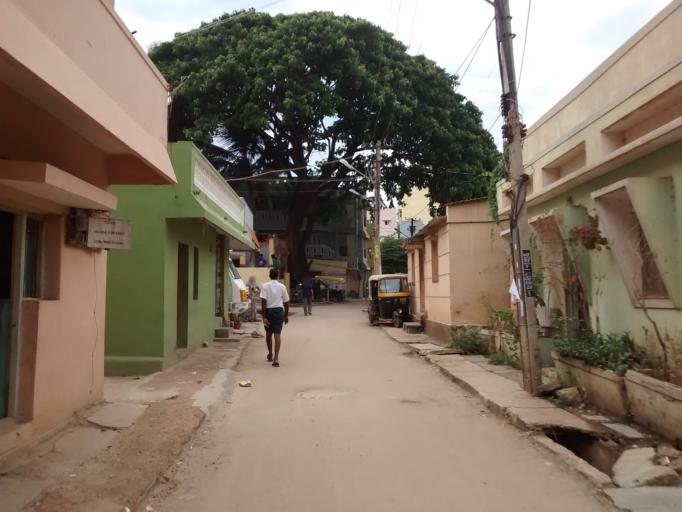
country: IN
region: Karnataka
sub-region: Bangalore Urban
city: Bangalore
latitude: 12.9460
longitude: 77.6804
